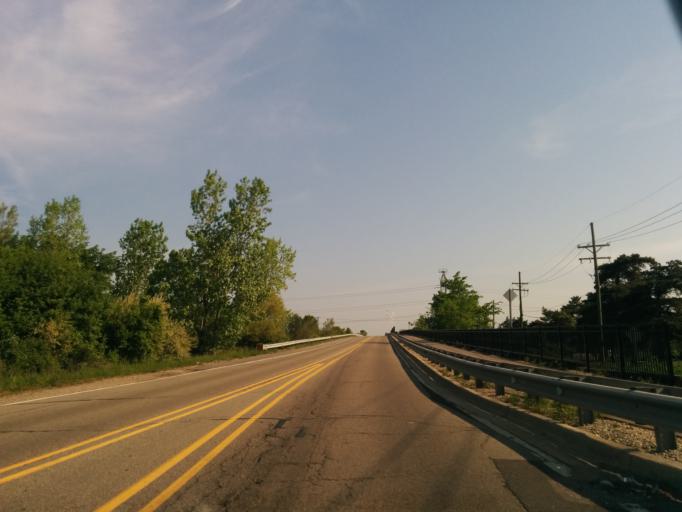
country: US
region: Michigan
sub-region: Oakland County
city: Novi
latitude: 42.4829
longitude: -83.4559
